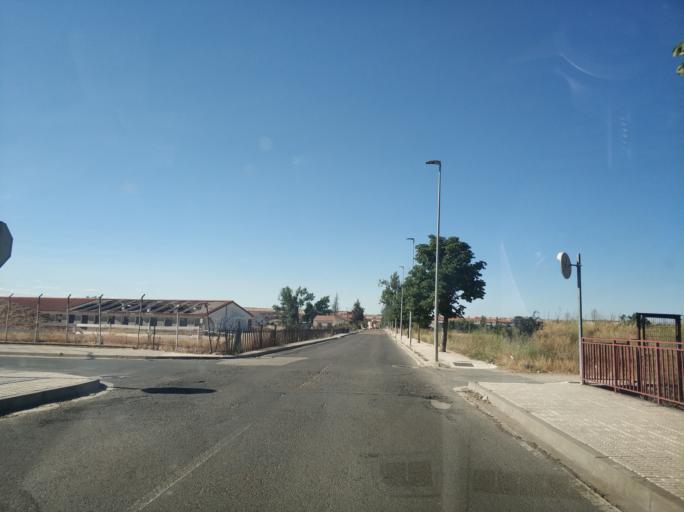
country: ES
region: Castille and Leon
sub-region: Provincia de Salamanca
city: Santa Marta de Tormes
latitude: 40.9449
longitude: -5.6206
